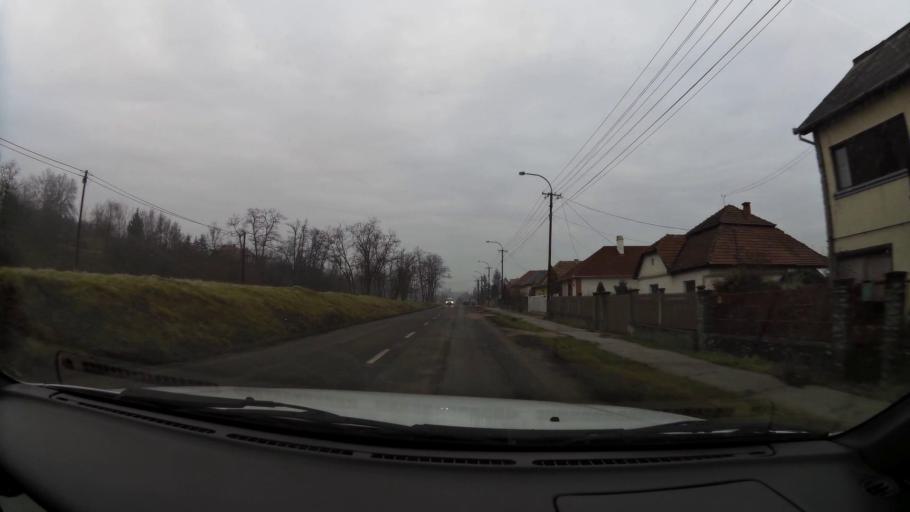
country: HU
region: Borsod-Abauj-Zemplen
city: Izsofalva
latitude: 48.3132
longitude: 20.6521
